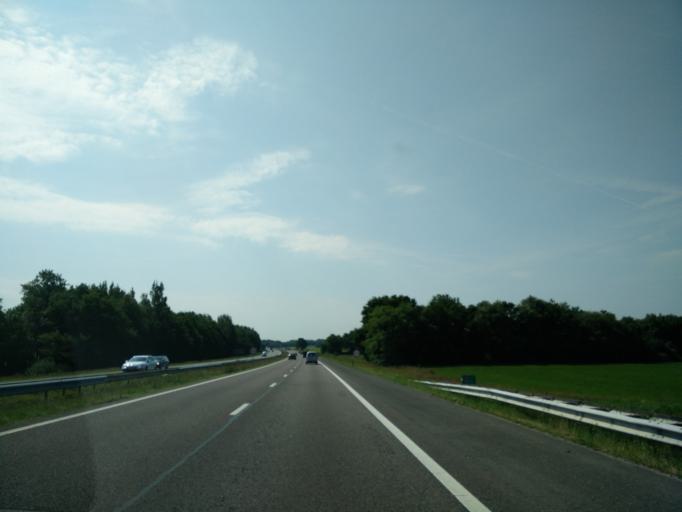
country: NL
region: Drenthe
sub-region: Gemeente Tynaarlo
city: Tynaarlo
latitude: 53.0778
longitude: 6.6034
